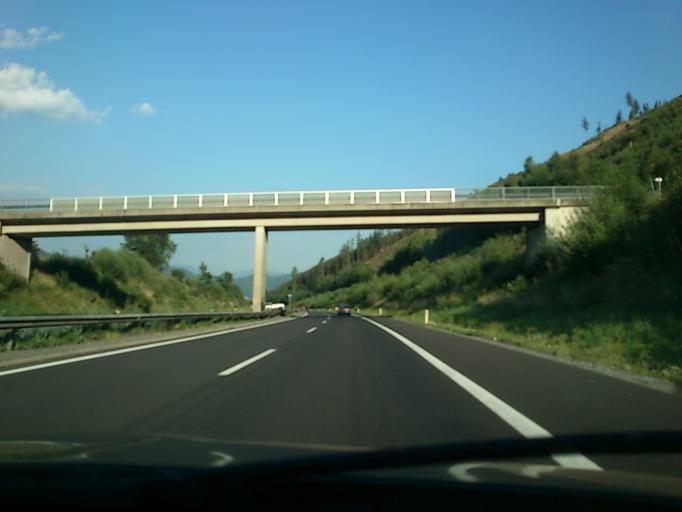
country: AT
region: Styria
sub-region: Politischer Bezirk Leoben
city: Kammern im Liesingtal
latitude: 47.3850
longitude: 14.9212
